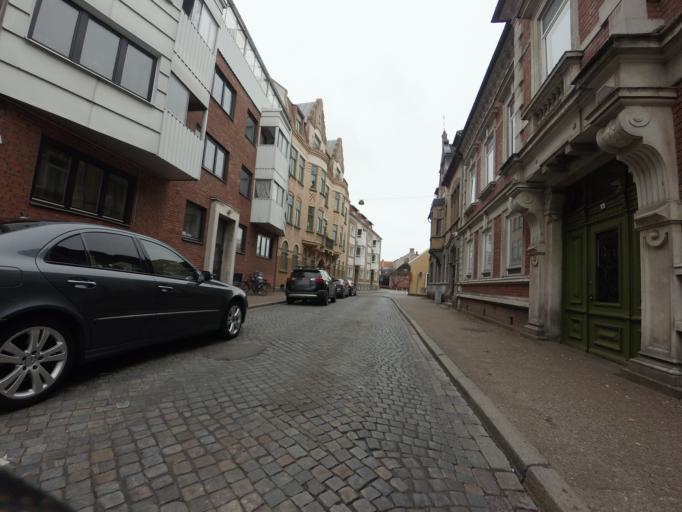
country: SE
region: Skane
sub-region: Ystads Kommun
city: Ystad
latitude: 55.4304
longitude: 13.8192
